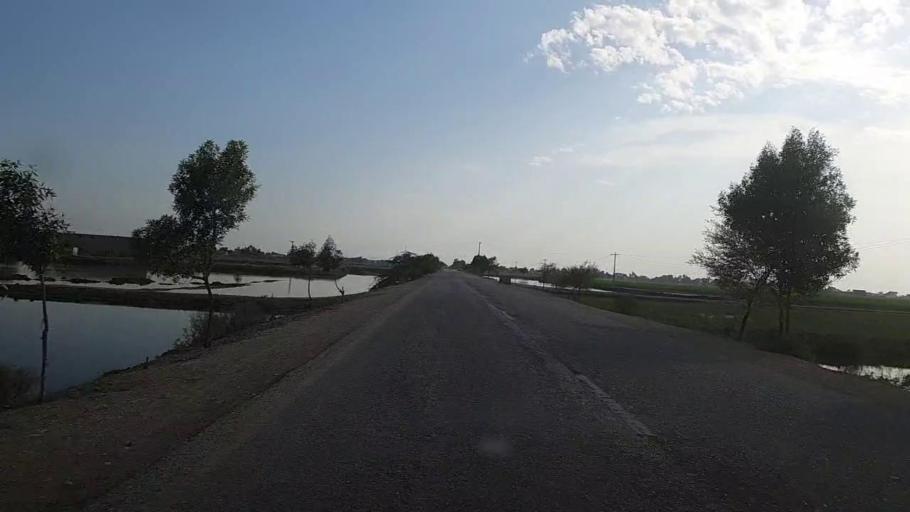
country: PK
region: Sindh
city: Thul
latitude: 28.1987
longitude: 68.7393
